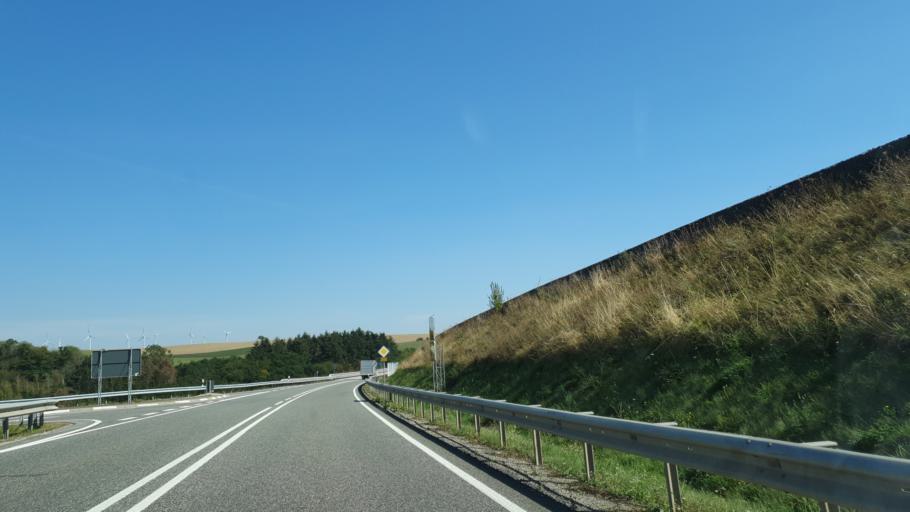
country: DE
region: Rheinland-Pfalz
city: Uhler
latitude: 50.0786
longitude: 7.4383
